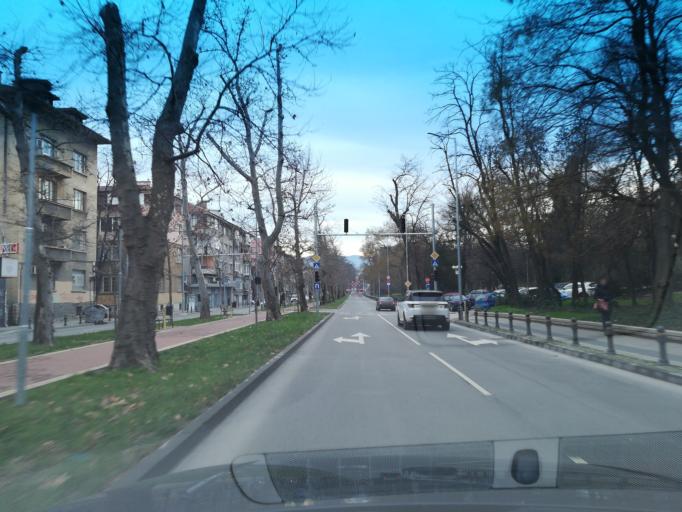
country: BG
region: Plovdiv
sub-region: Obshtina Plovdiv
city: Plovdiv
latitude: 42.1449
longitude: 24.7411
